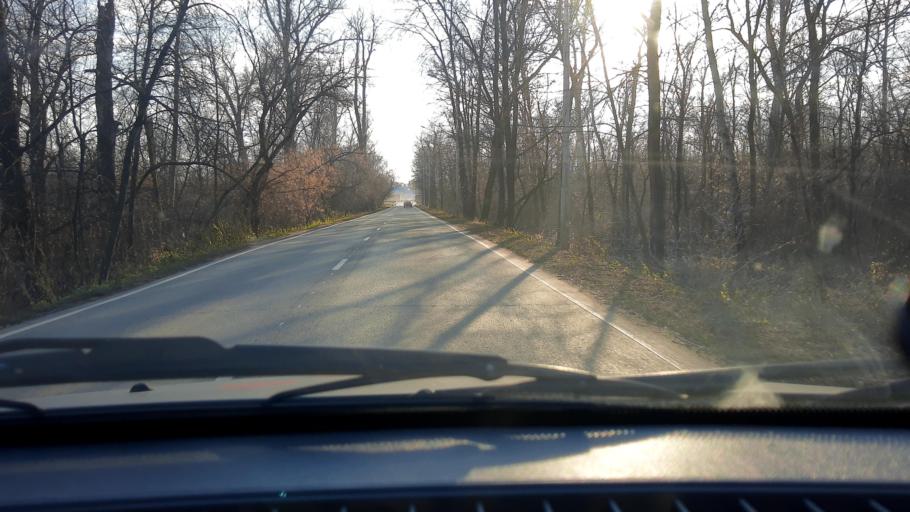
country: RU
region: Bashkortostan
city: Ufa
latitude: 54.6607
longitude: 55.9358
